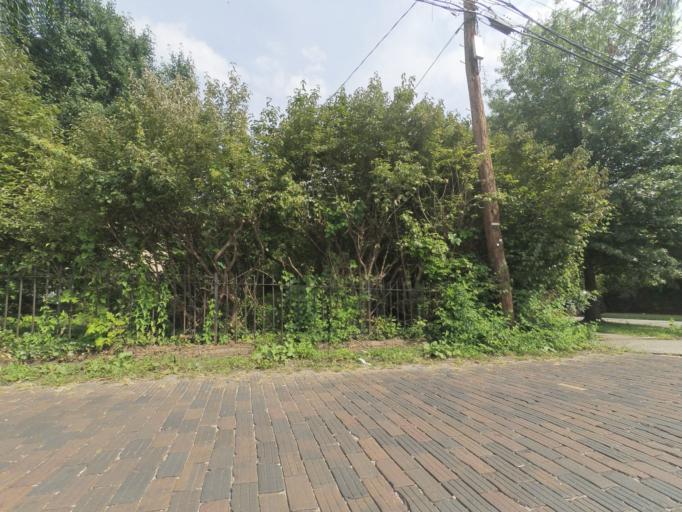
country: US
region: West Virginia
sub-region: Cabell County
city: Huntington
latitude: 38.4204
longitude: -82.4332
